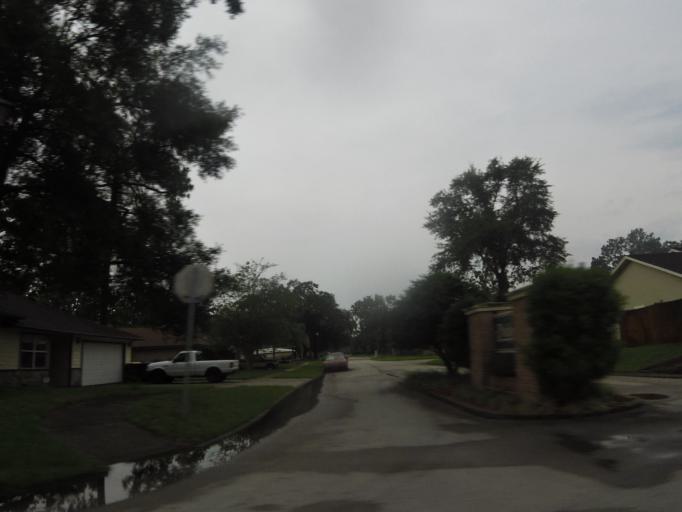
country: US
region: Florida
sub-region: Duval County
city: Jacksonville
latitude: 30.2717
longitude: -81.5764
